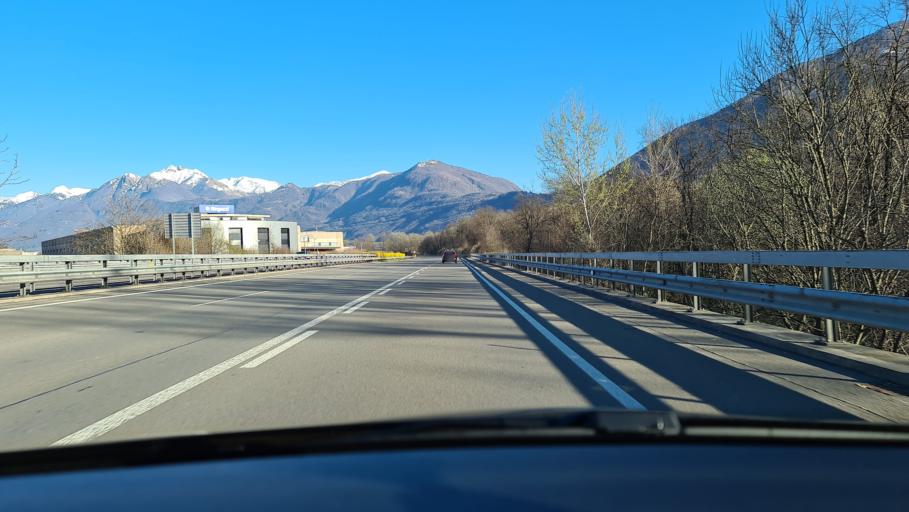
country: CH
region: Ticino
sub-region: Locarno District
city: Gordola
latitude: 46.1720
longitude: 8.8598
